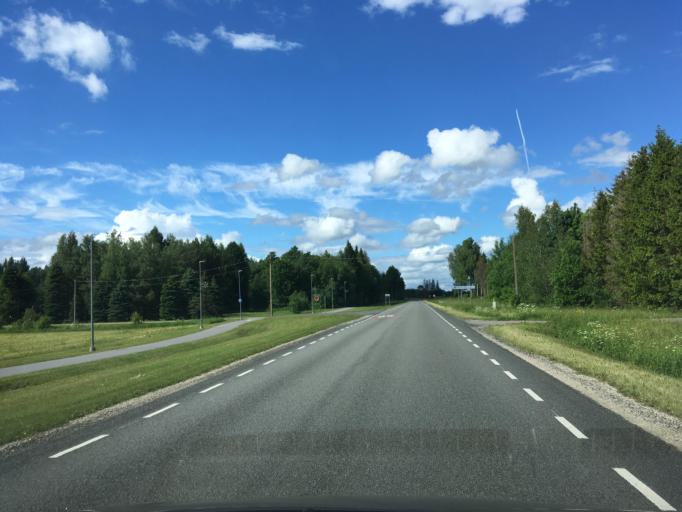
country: EE
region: Paernumaa
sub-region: Halinga vald
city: Parnu-Jaagupi
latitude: 58.6157
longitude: 24.5076
